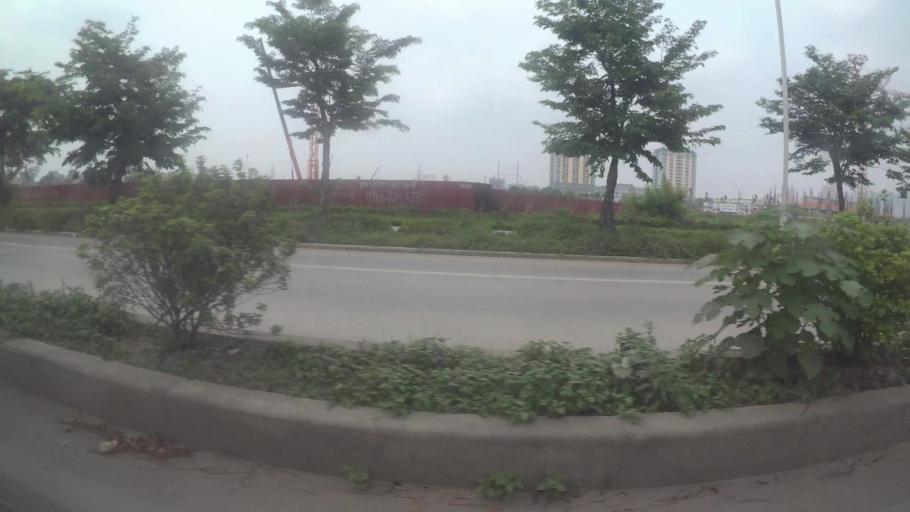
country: VN
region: Ha Noi
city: Cau Dien
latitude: 21.0377
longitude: 105.7470
